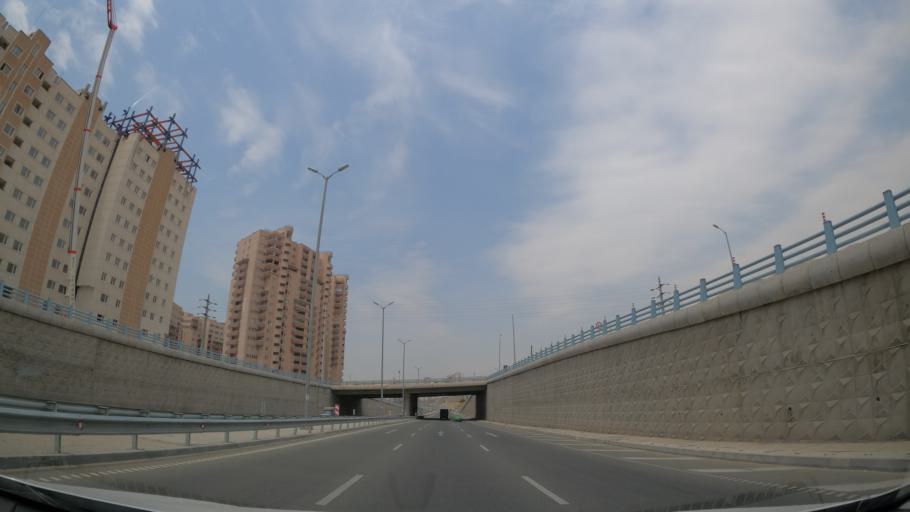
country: IR
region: Tehran
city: Shahr-e Qods
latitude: 35.7517
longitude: 51.1553
